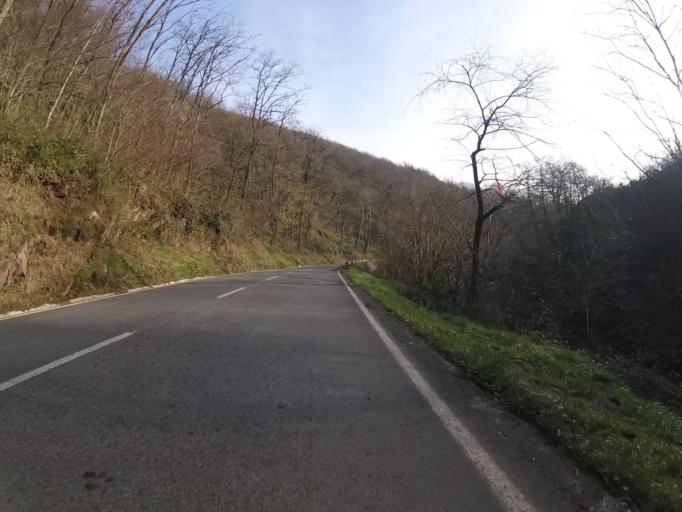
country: ES
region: Navarre
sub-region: Provincia de Navarra
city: Areso
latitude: 43.0955
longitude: -1.9423
